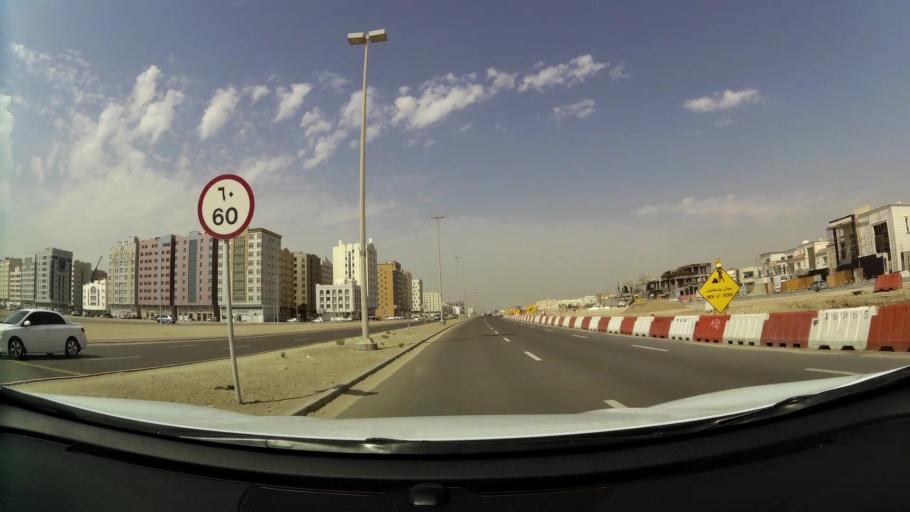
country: AE
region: Abu Dhabi
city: Abu Dhabi
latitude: 24.3167
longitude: 54.5396
